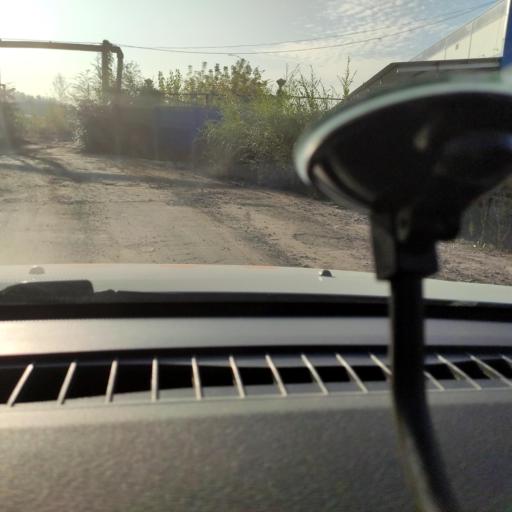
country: RU
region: Samara
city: Samara
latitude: 53.1865
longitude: 50.2616
